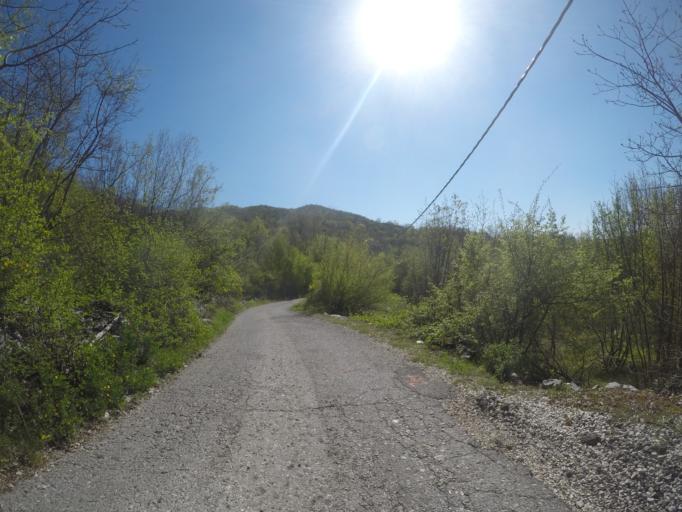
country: ME
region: Danilovgrad
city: Danilovgrad
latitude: 42.5259
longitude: 19.0466
